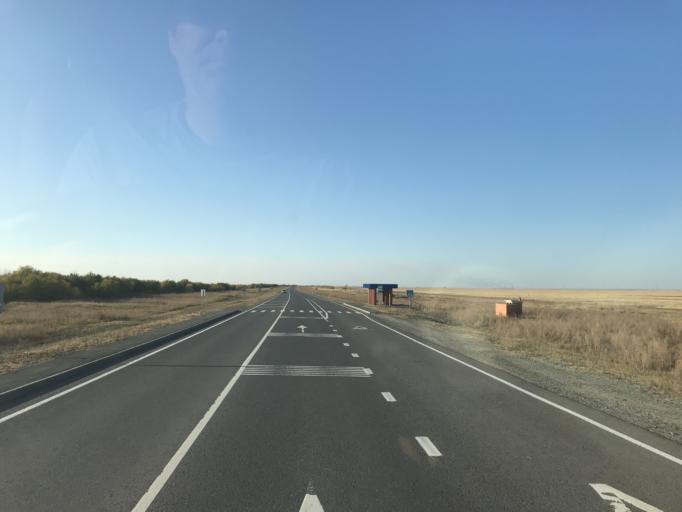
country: KZ
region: Pavlodar
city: Aksu
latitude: 52.0193
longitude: 77.2312
